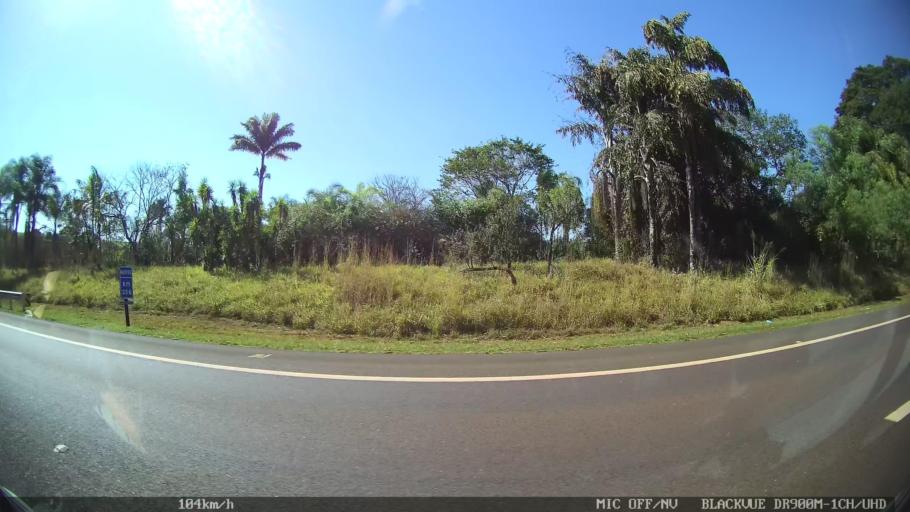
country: BR
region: Sao Paulo
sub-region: Batatais
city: Batatais
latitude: -20.8467
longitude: -47.6012
